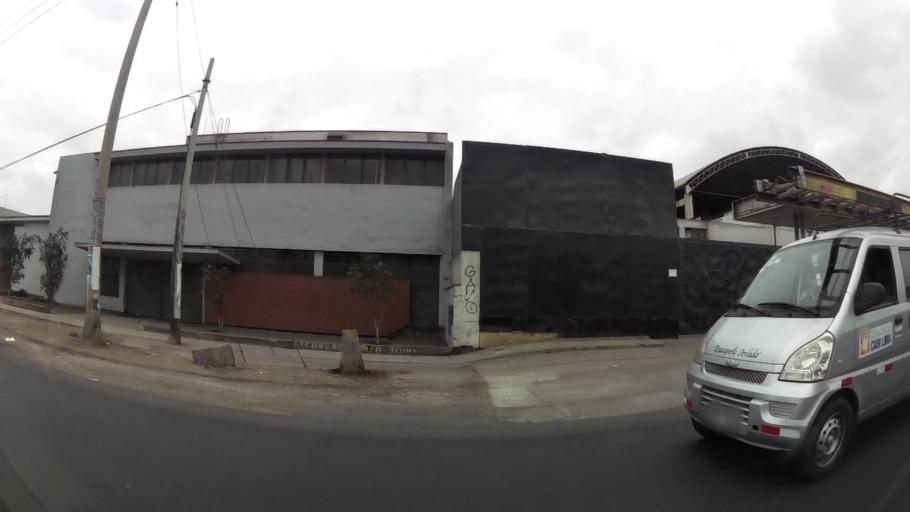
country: PE
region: Lima
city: Lima
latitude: -12.0451
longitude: -77.0619
